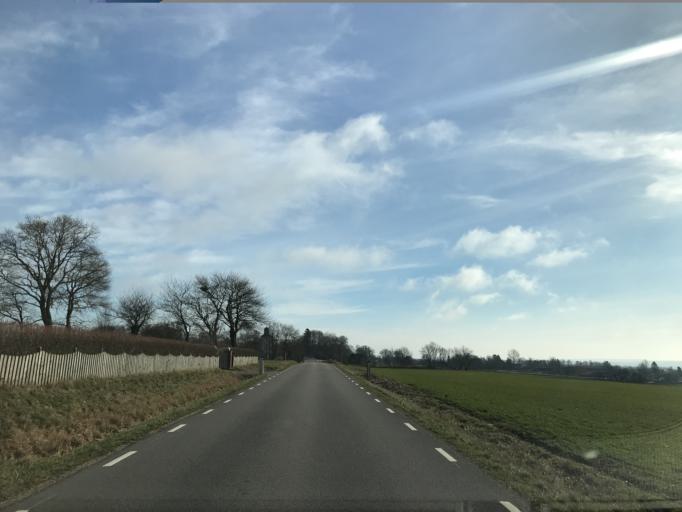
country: SE
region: Skane
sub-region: Hoors Kommun
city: Loberod
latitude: 55.7251
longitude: 13.5198
